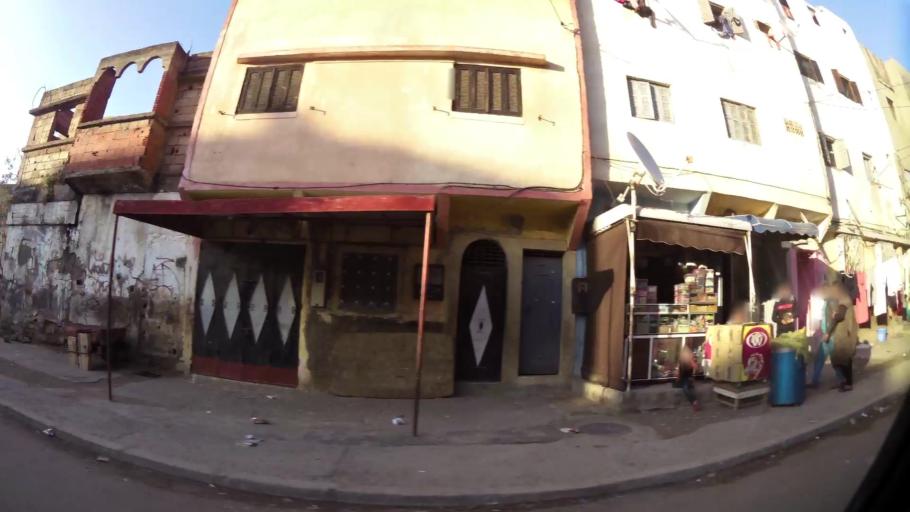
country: MA
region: Chaouia-Ouardigha
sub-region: Settat Province
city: Settat
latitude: 32.9981
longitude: -7.6079
